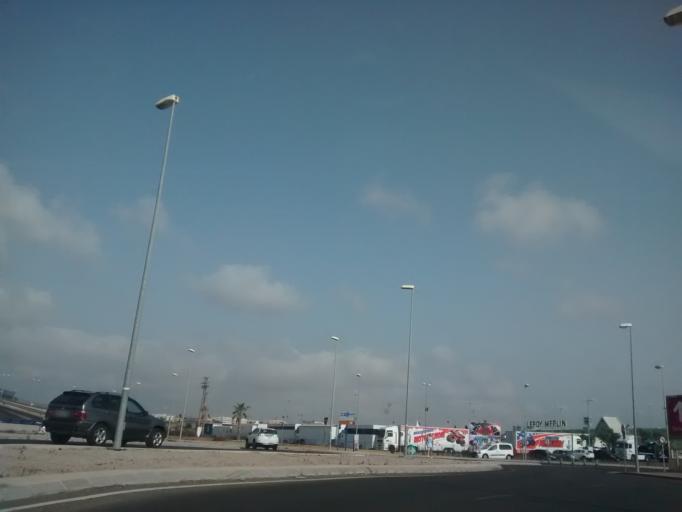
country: ES
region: Valencia
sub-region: Provincia de Alicante
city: Torrevieja
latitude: 37.9266
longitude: -0.7358
